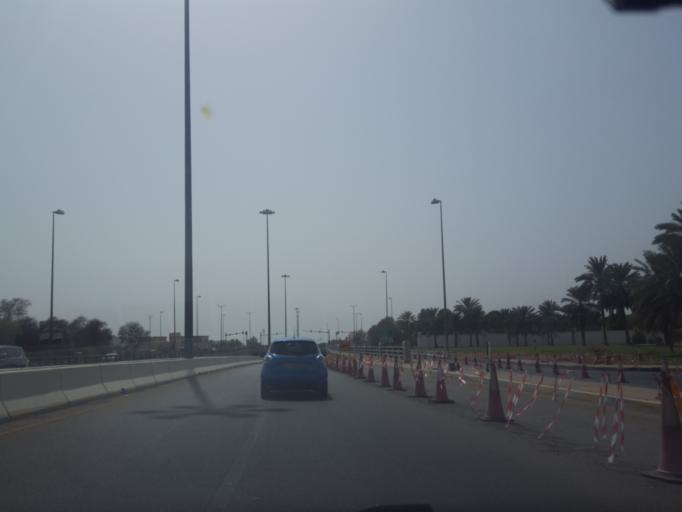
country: AE
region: Abu Dhabi
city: Al Ain
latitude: 24.2059
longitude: 55.7854
